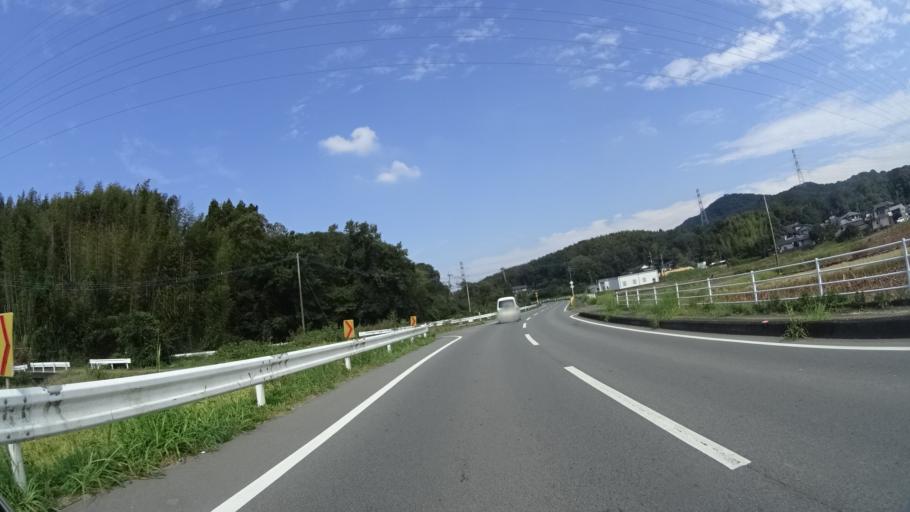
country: JP
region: Kumamoto
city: Matsubase
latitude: 32.6554
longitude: 130.7159
